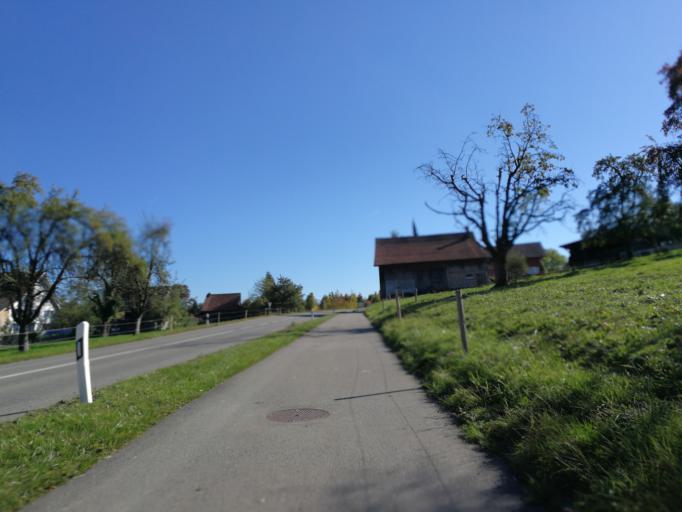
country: CH
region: Zurich
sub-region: Bezirk Uster
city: Egg
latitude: 47.2900
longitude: 8.6933
